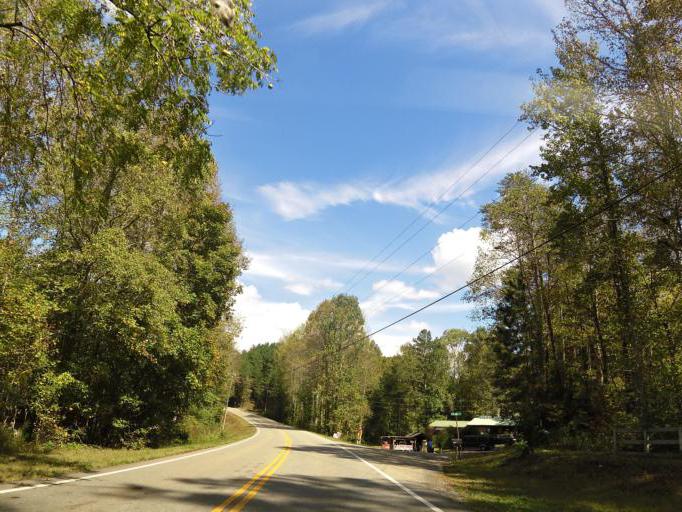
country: US
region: Georgia
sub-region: Pickens County
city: Jasper
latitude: 34.5446
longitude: -84.2614
